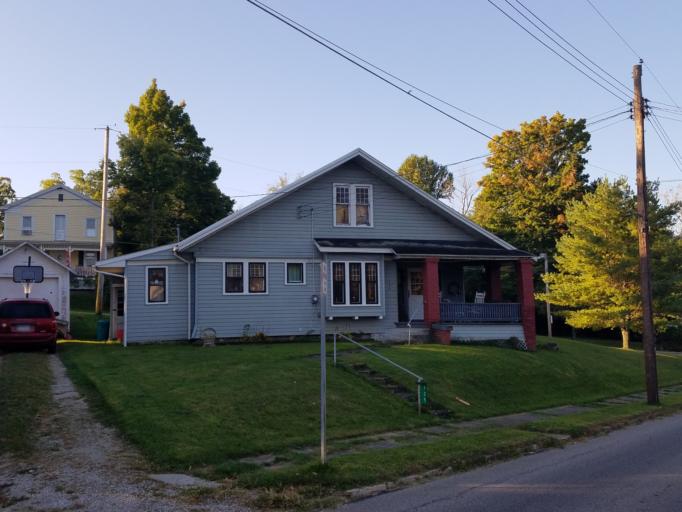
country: US
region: Ohio
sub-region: Morrow County
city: Mount Gilead
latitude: 40.5475
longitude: -82.8267
